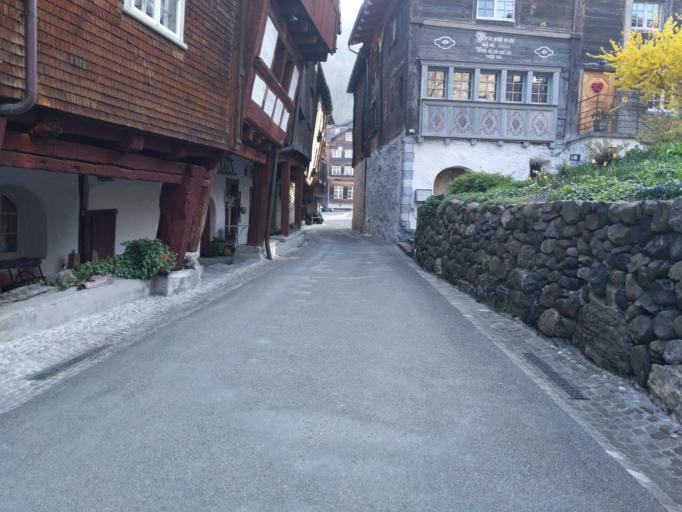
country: CH
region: Saint Gallen
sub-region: Wahlkreis Werdenberg
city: Buchs
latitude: 47.1682
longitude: 9.4630
